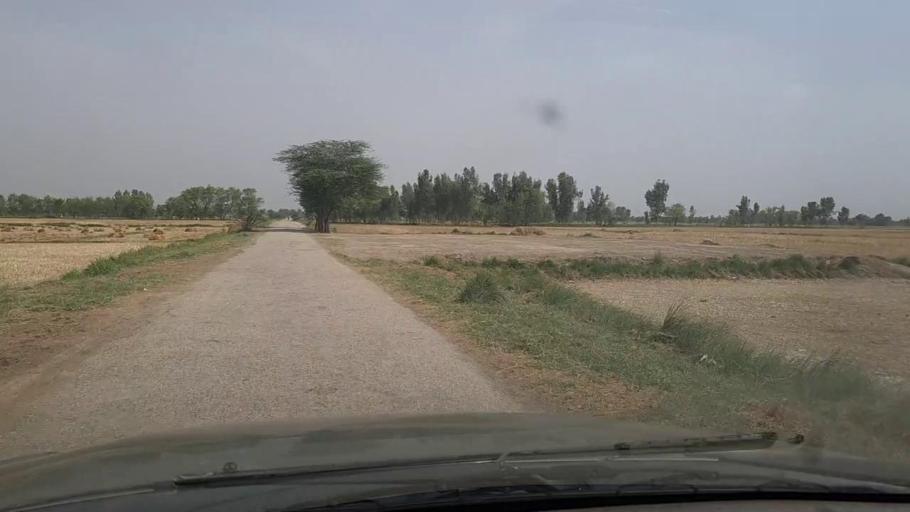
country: PK
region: Sindh
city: Lakhi
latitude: 27.8392
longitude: 68.7645
